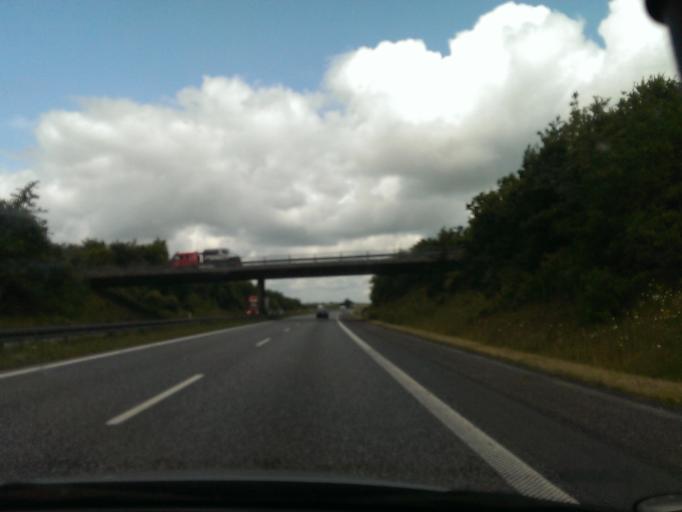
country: DK
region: North Denmark
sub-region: Mariagerfjord Kommune
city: Mariager
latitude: 56.5418
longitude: 9.9014
